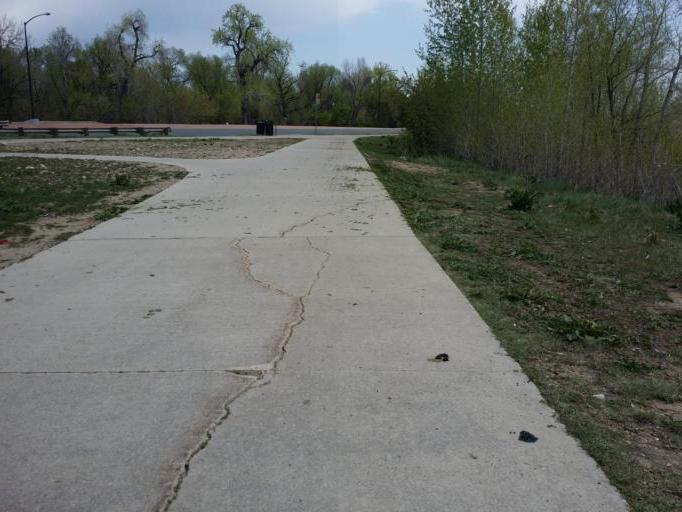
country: US
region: Colorado
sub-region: Boulder County
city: Boulder
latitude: 40.0142
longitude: -105.2449
